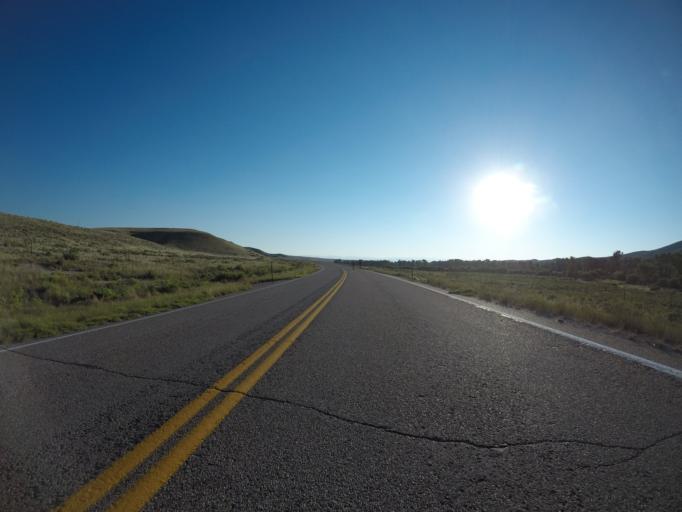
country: US
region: Wyoming
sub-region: Sublette County
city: Marbleton
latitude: 42.5792
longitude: -109.9254
